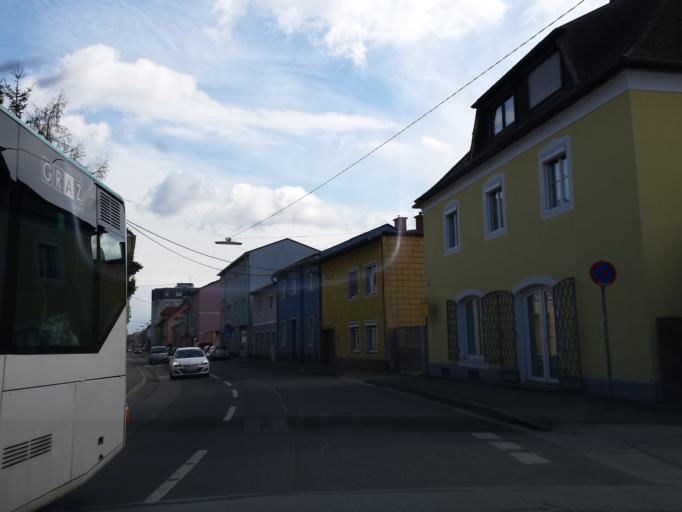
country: AT
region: Styria
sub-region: Graz Stadt
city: Goesting
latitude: 47.0923
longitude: 15.4139
